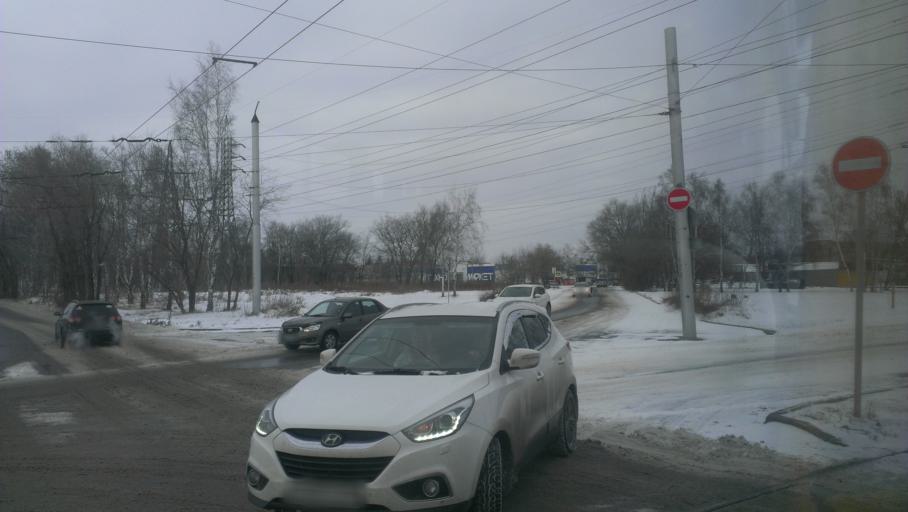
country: RU
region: Altai Krai
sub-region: Gorod Barnaulskiy
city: Barnaul
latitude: 53.3860
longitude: 83.7130
